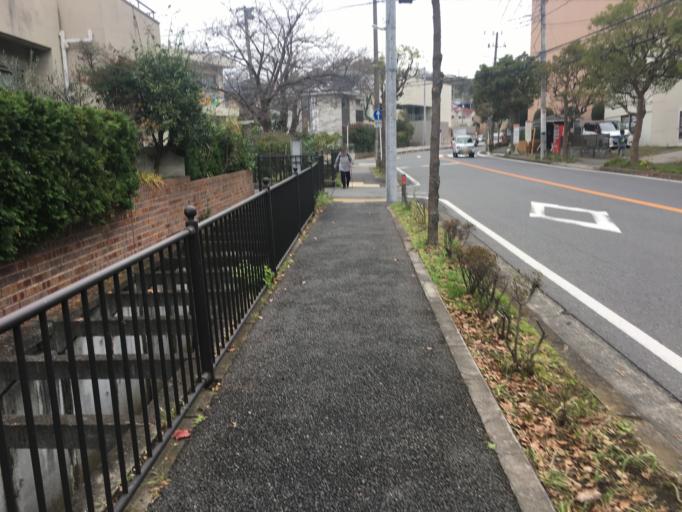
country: JP
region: Kanagawa
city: Kamakura
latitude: 35.3276
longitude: 139.5253
